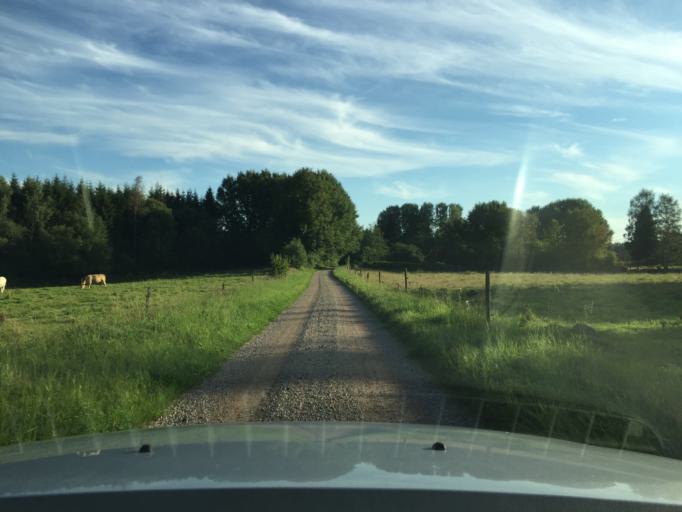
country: SE
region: Skane
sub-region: Hassleholms Kommun
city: Sosdala
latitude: 56.0174
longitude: 13.7092
